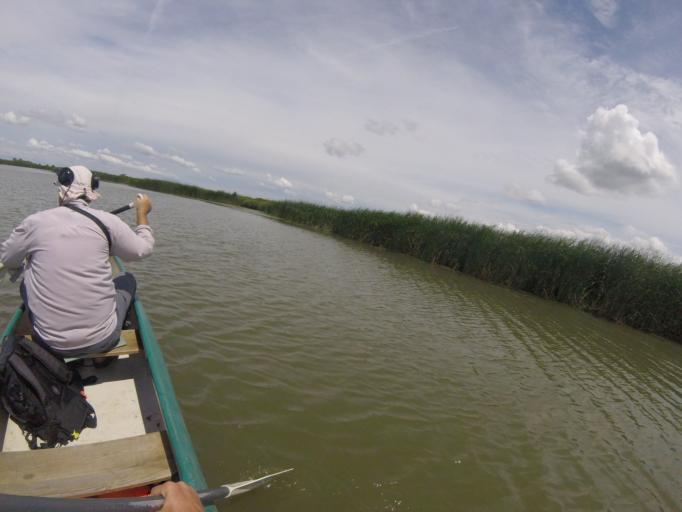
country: HU
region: Heves
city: Poroszlo
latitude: 47.5912
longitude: 20.6326
